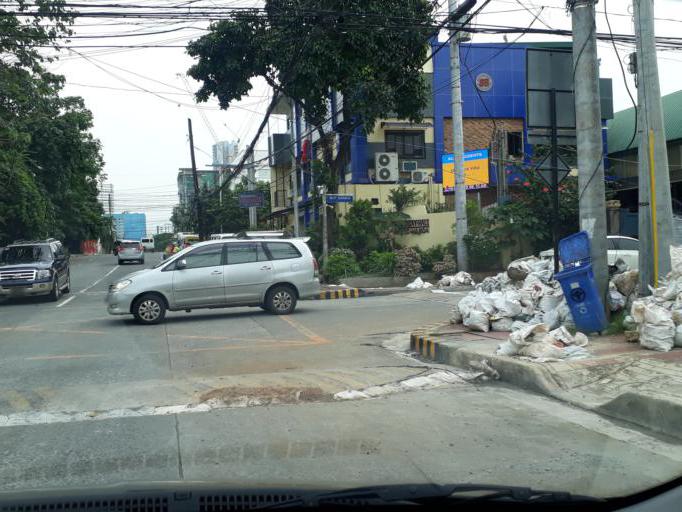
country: PH
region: Calabarzon
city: Del Monte
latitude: 14.6320
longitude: 121.0325
